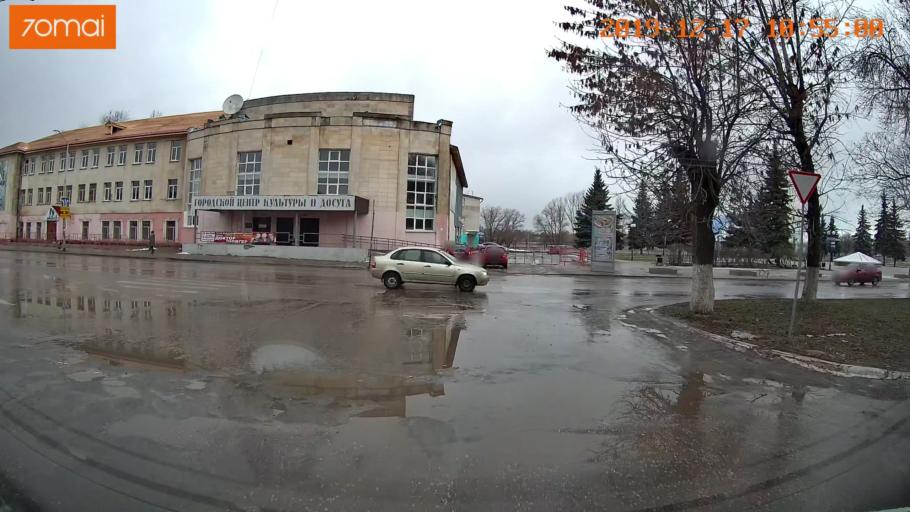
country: RU
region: Vladimir
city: Gus'-Khrustal'nyy
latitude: 55.6156
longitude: 40.6724
